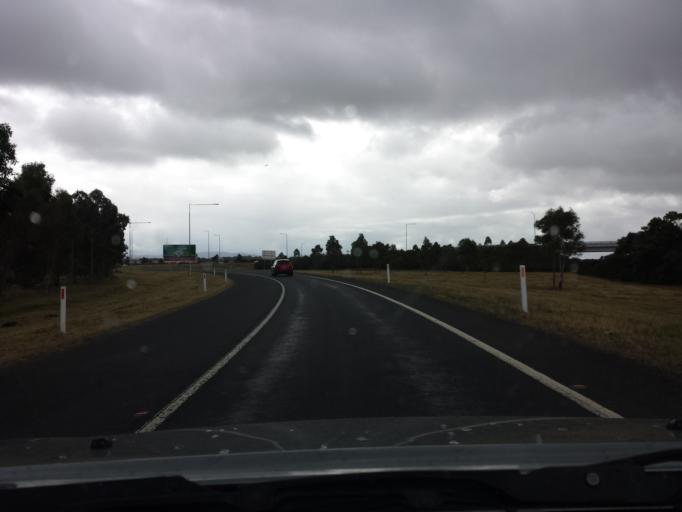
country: AU
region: Victoria
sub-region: Cardinia
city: Pakenham South
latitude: -38.0916
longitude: 145.4877
